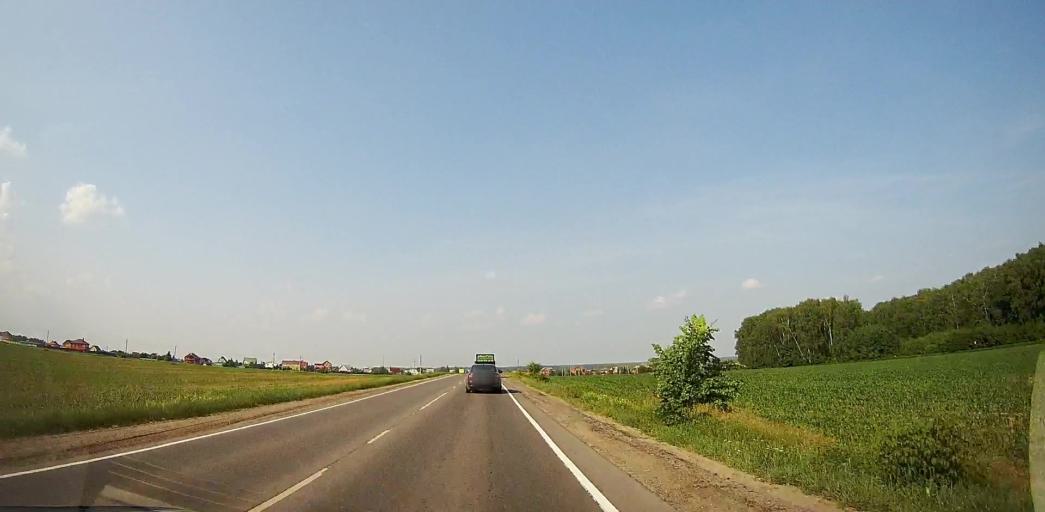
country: RU
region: Moskovskaya
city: Zhitnevo
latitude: 55.3328
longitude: 37.9059
